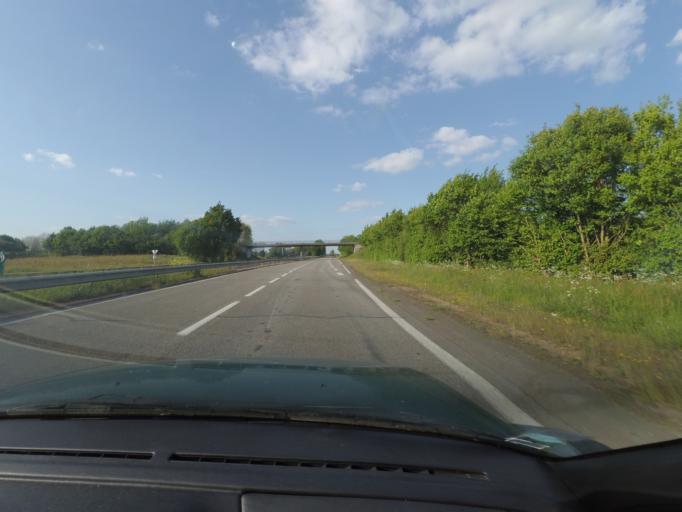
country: FR
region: Pays de la Loire
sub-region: Departement de la Vendee
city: Saligny
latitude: 46.8397
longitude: -1.4194
